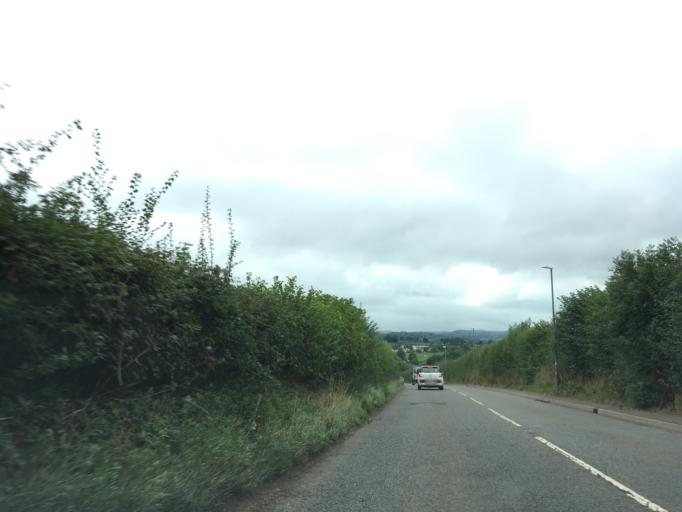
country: GB
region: England
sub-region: Bath and North East Somerset
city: Paulton
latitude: 51.3181
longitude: -2.5147
